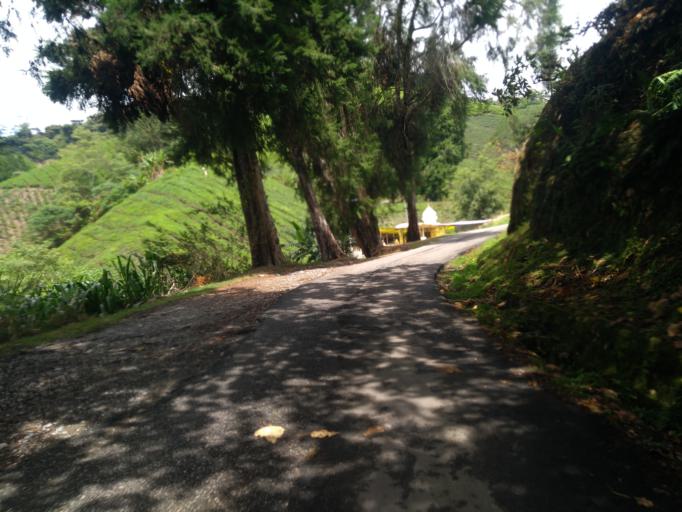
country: MY
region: Pahang
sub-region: Cameron Highlands
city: Tanah Rata
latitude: 4.5210
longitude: 101.4014
